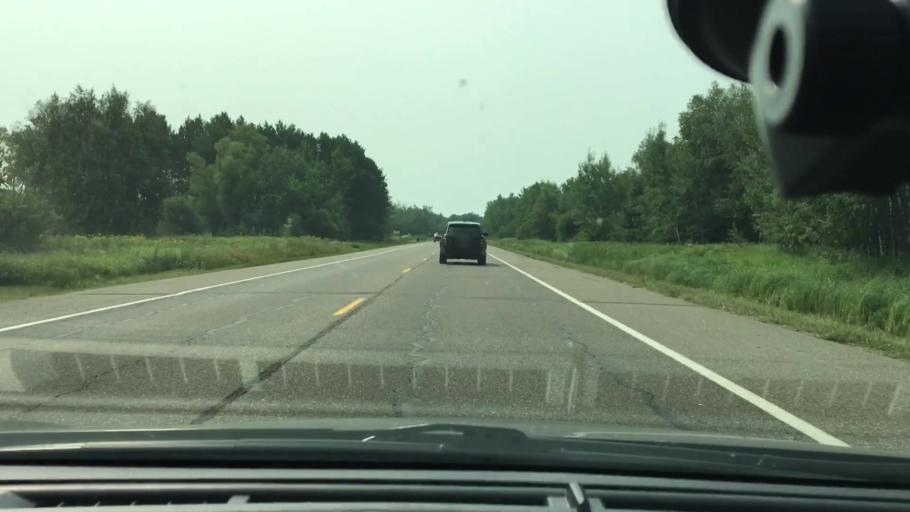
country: US
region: Minnesota
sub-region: Crow Wing County
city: Brainerd
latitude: 46.3907
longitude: -94.2233
